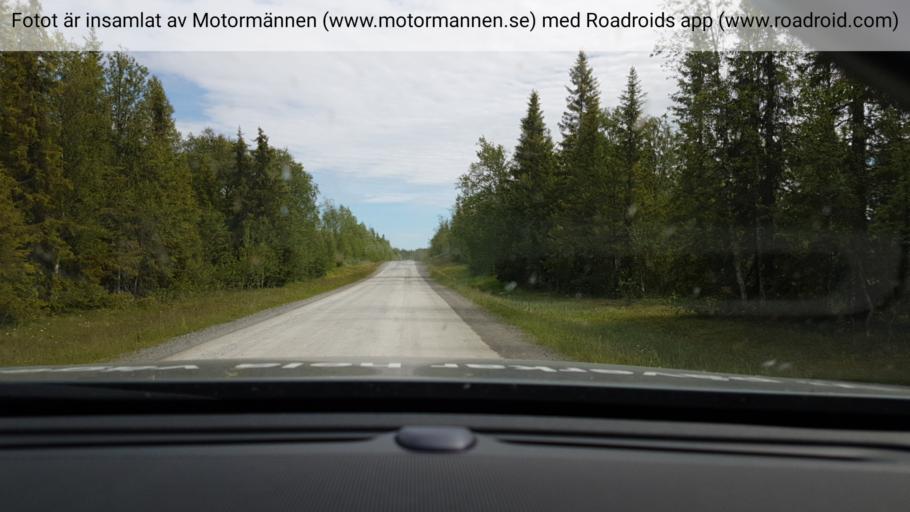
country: SE
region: Vaesterbotten
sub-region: Vilhelmina Kommun
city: Sjoberg
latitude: 65.1931
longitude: 16.1823
